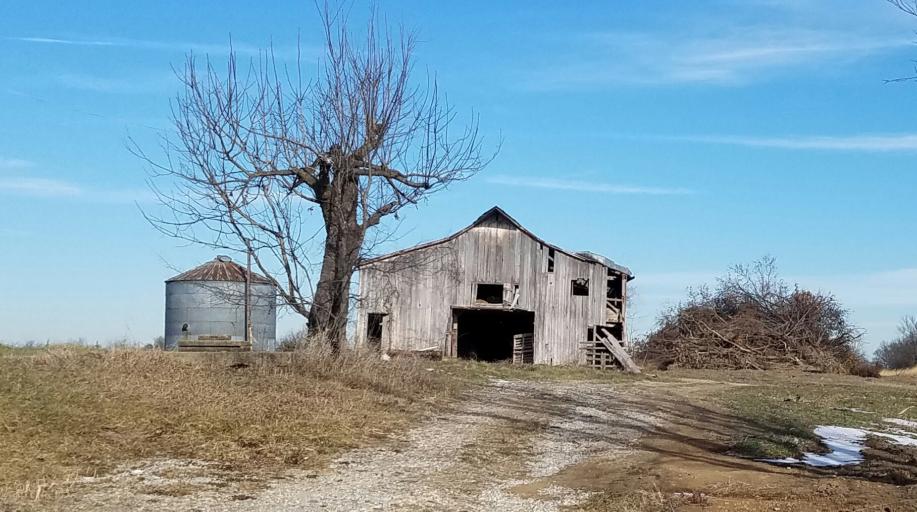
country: US
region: Missouri
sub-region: Moniteau County
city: Tipton
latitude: 38.6454
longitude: -92.6929
